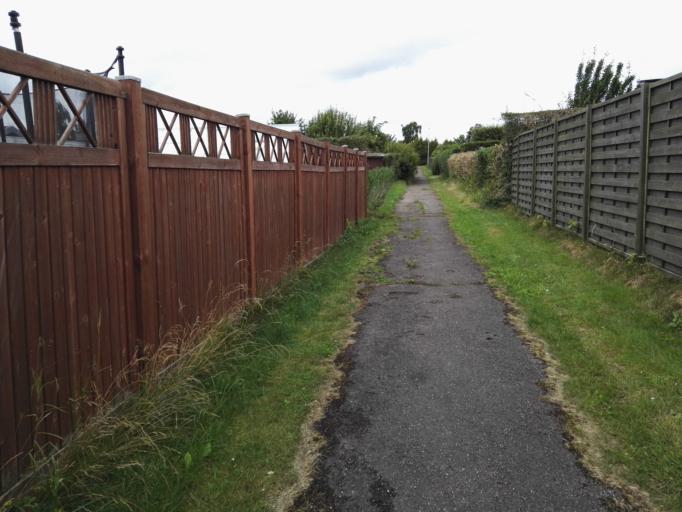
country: DK
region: Capital Region
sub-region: Egedal Kommune
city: Stenlose
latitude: 55.7679
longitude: 12.1766
